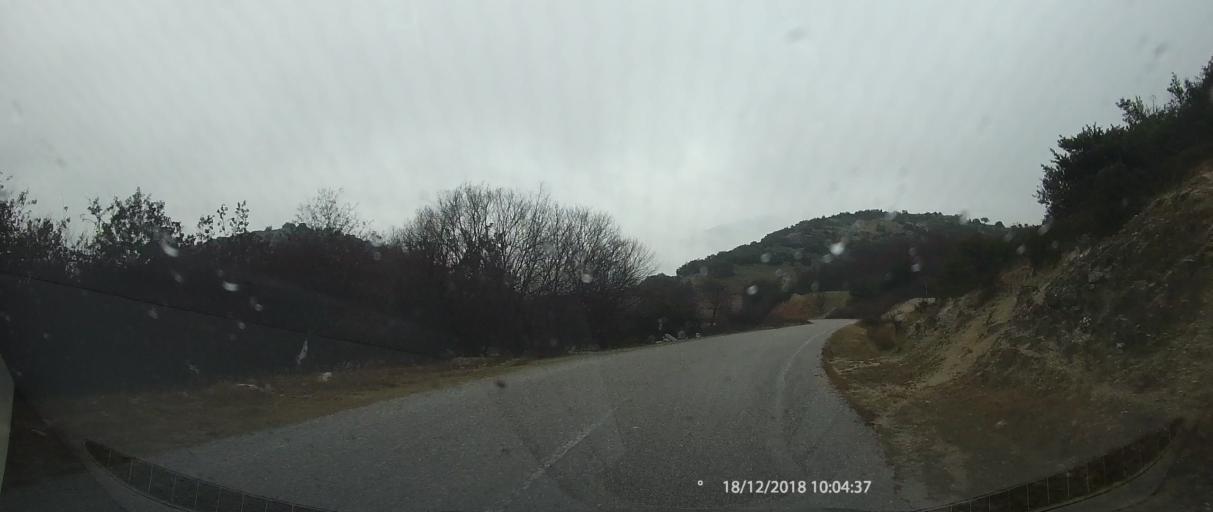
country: GR
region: Thessaly
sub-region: Nomos Larisis
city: Livadi
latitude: 40.0542
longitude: 22.2224
